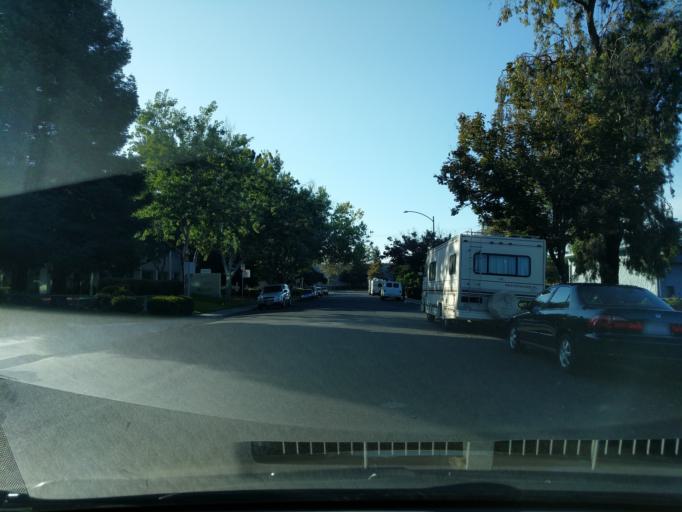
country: US
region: California
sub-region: Santa Clara County
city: Los Altos
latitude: 37.3999
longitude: -122.1073
